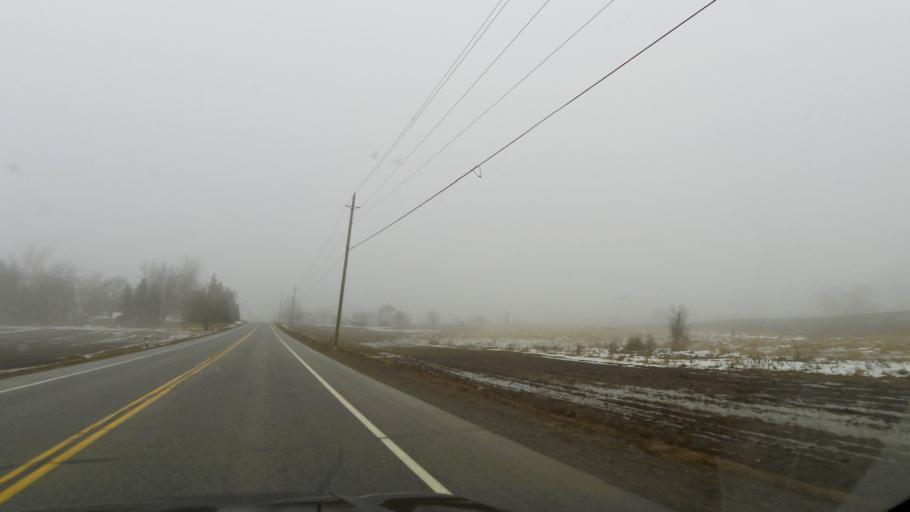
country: CA
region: Ontario
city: Brampton
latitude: 43.8520
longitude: -79.8583
